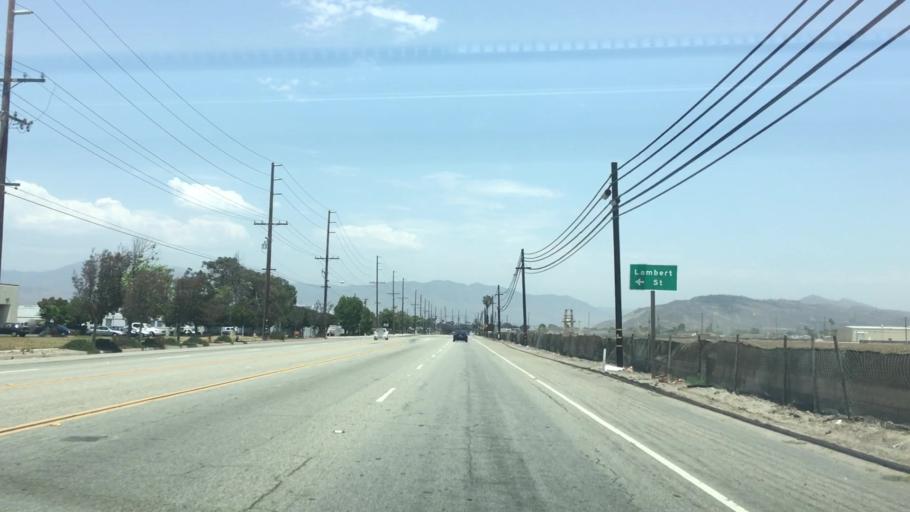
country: US
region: California
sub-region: Ventura County
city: El Rio
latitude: 34.2512
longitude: -119.1585
